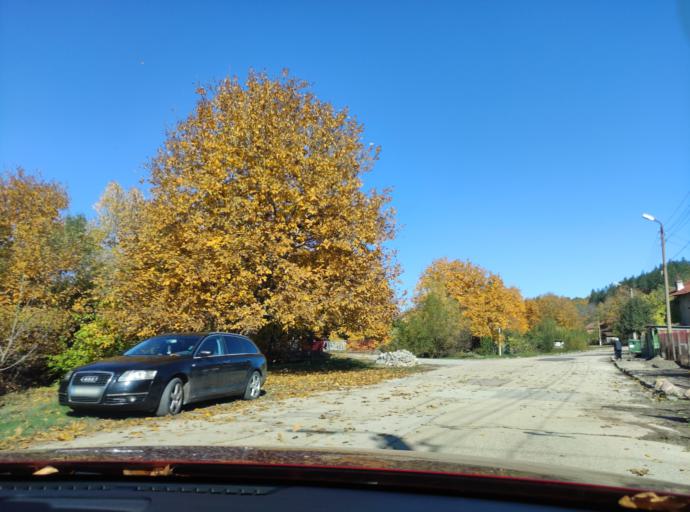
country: BG
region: Montana
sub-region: Obshtina Montana
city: Montana
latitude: 43.4157
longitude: 23.0665
